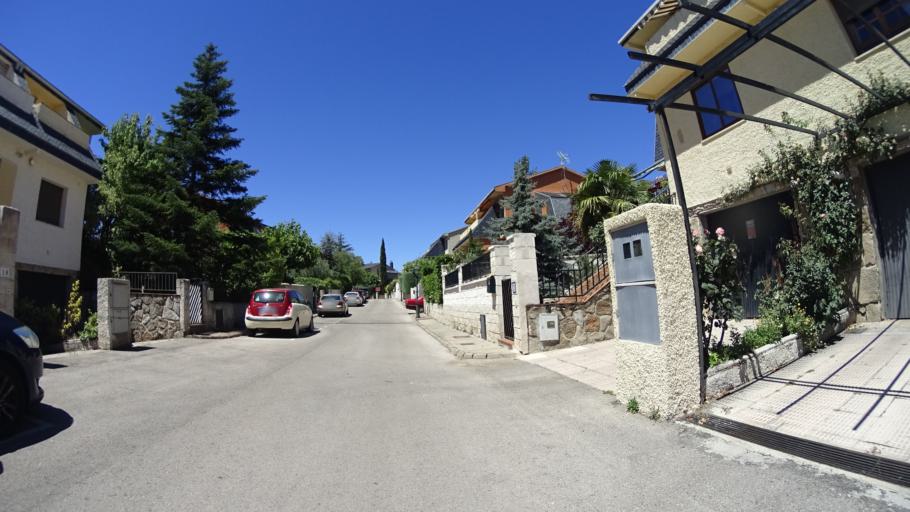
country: ES
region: Madrid
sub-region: Provincia de Madrid
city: Collado Mediano
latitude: 40.6904
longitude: -4.0273
